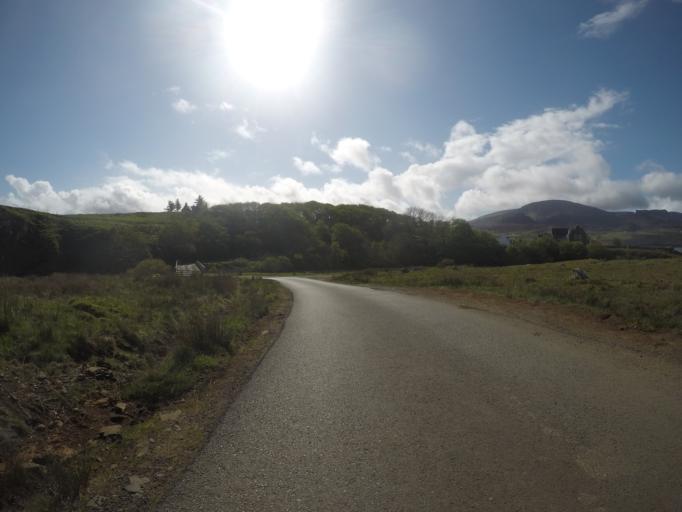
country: GB
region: Scotland
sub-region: Highland
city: Portree
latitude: 57.6334
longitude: -6.2145
